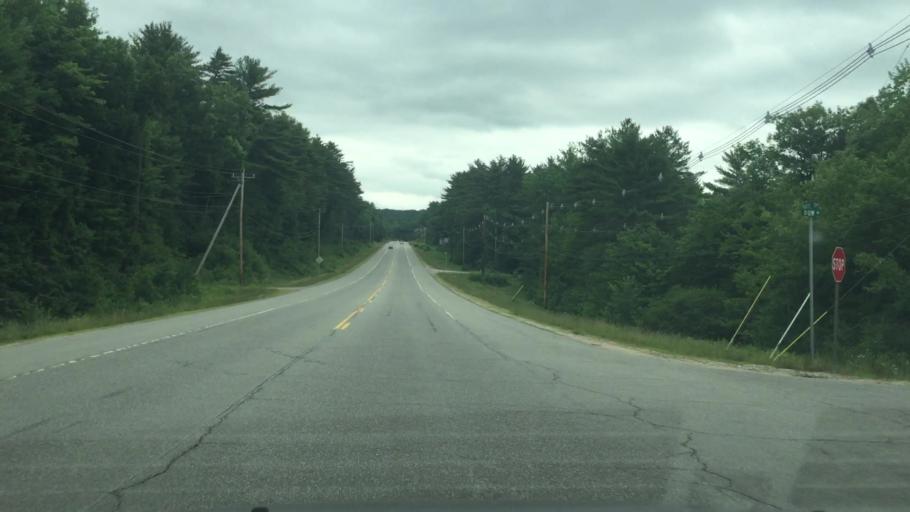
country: US
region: New Hampshire
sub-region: Belknap County
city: Meredith
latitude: 43.6236
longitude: -71.5435
